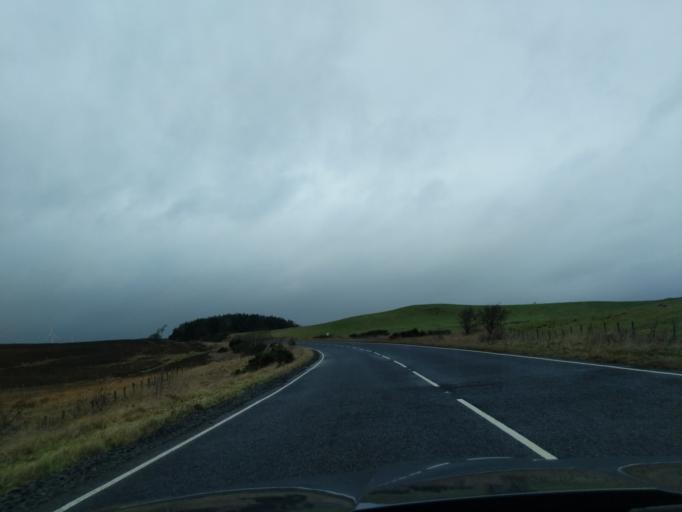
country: GB
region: England
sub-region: Northumberland
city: Rothley
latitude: 55.1738
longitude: -2.0264
